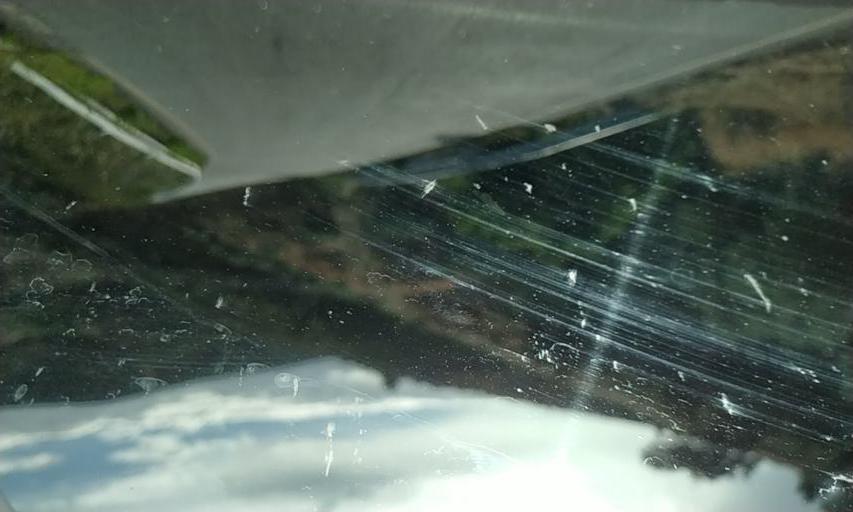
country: PT
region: Viseu
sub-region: Sao Joao da Pesqueira
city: Sao Joao da Pesqueira
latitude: 41.1083
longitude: -7.4669
